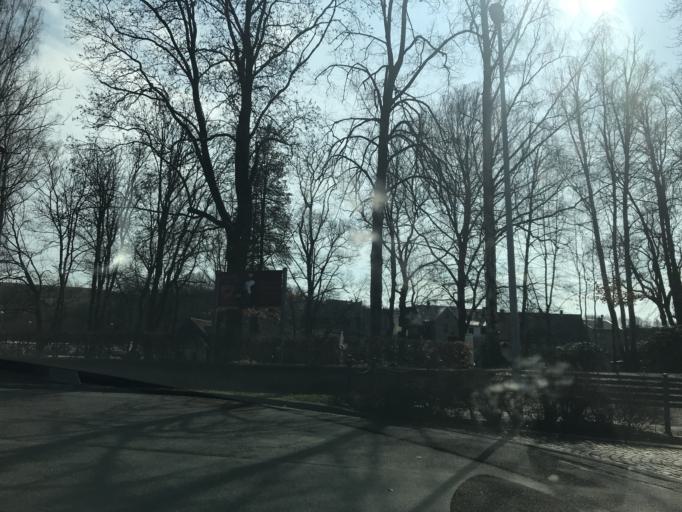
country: DE
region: Saxony
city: Rochlitz
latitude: 51.0468
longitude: 12.8066
